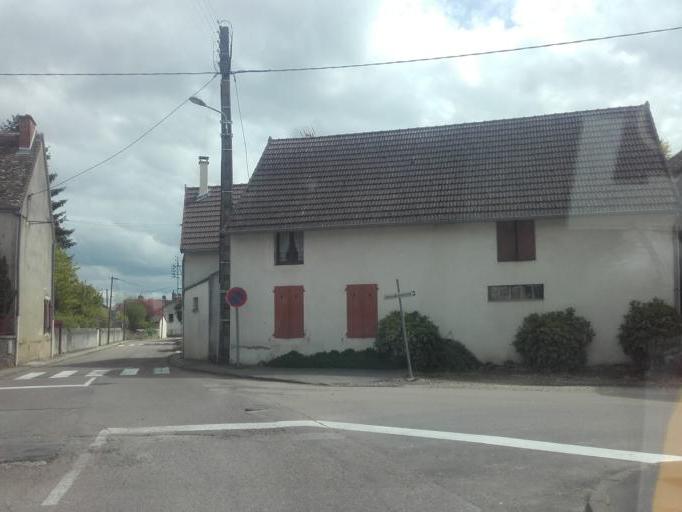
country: FR
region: Bourgogne
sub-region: Departement de Saone-et-Loire
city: Saint-Remy
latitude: 46.7685
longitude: 4.8150
